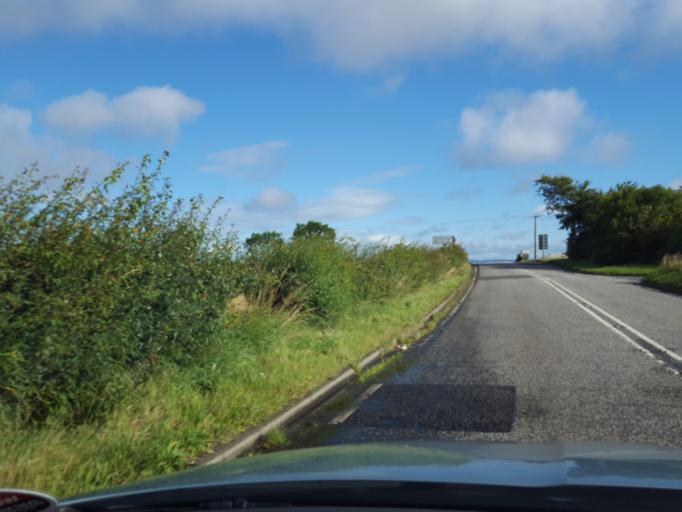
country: GB
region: Scotland
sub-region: West Lothian
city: Broxburn
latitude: 55.9530
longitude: -3.5098
